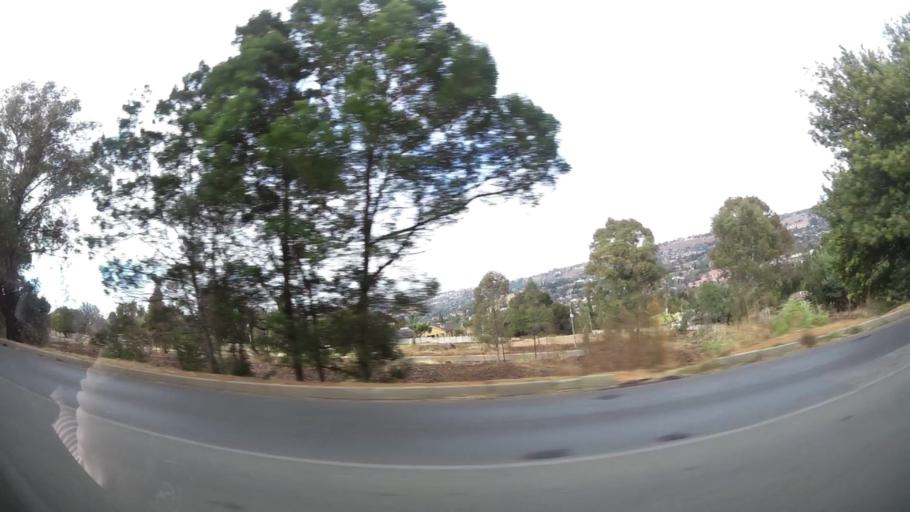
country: ZA
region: Gauteng
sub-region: City of Johannesburg Metropolitan Municipality
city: Roodepoort
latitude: -26.1074
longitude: 27.8645
